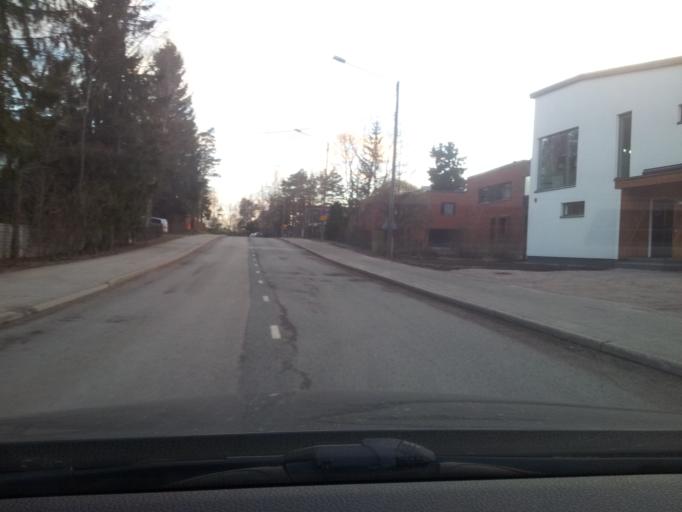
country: FI
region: Uusimaa
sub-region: Helsinki
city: Koukkuniemi
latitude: 60.1765
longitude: 24.7689
